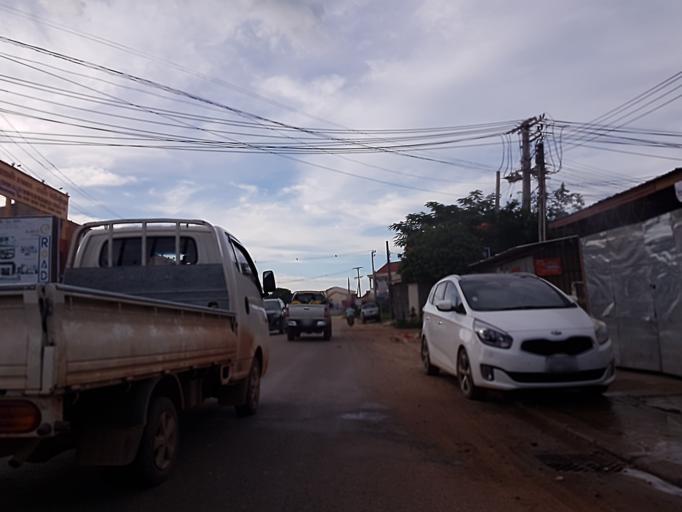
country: LA
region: Vientiane
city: Vientiane
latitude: 17.9928
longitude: 102.5720
